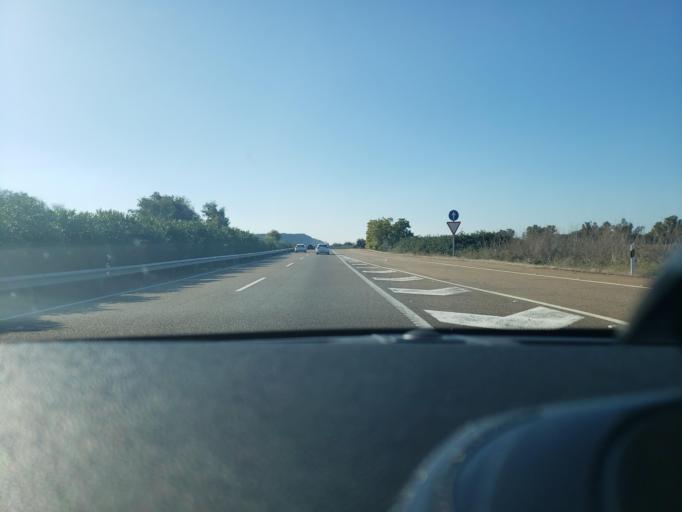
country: ES
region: Extremadura
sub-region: Provincia de Badajoz
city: Torremayor
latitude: 38.8609
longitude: -6.5483
